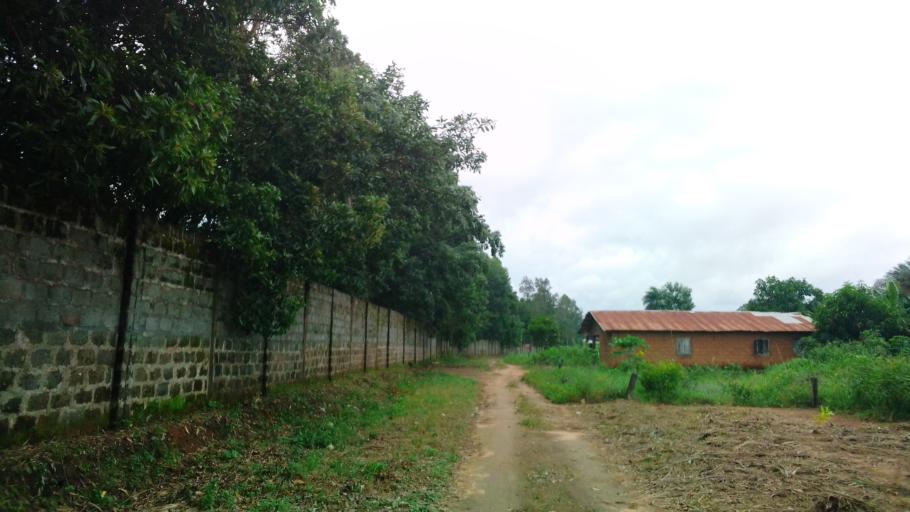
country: SL
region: Northern Province
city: Lunsar
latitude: 8.6956
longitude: -12.5492
